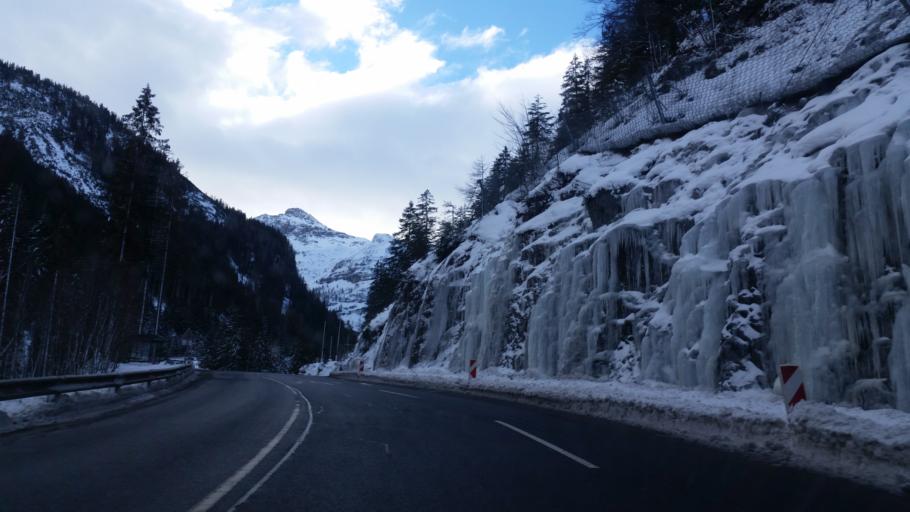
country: AT
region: Salzburg
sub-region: Politischer Bezirk Sankt Johann im Pongau
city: Untertauern
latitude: 47.2707
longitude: 13.5002
